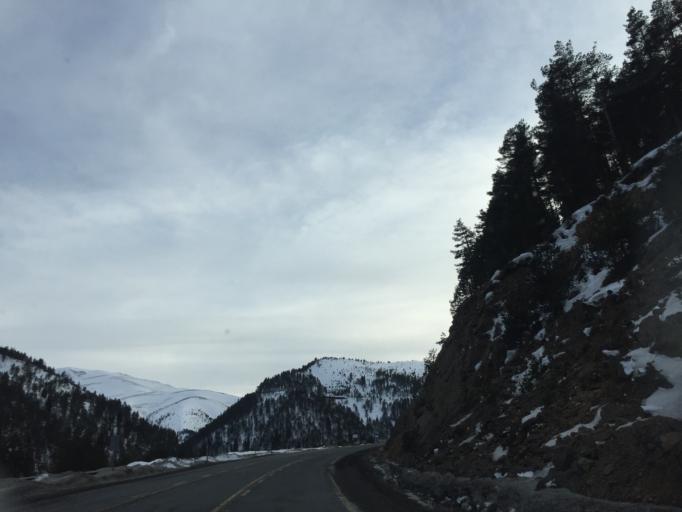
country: TR
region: Gumushane
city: Yaglidere
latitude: 40.6641
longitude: 39.4156
